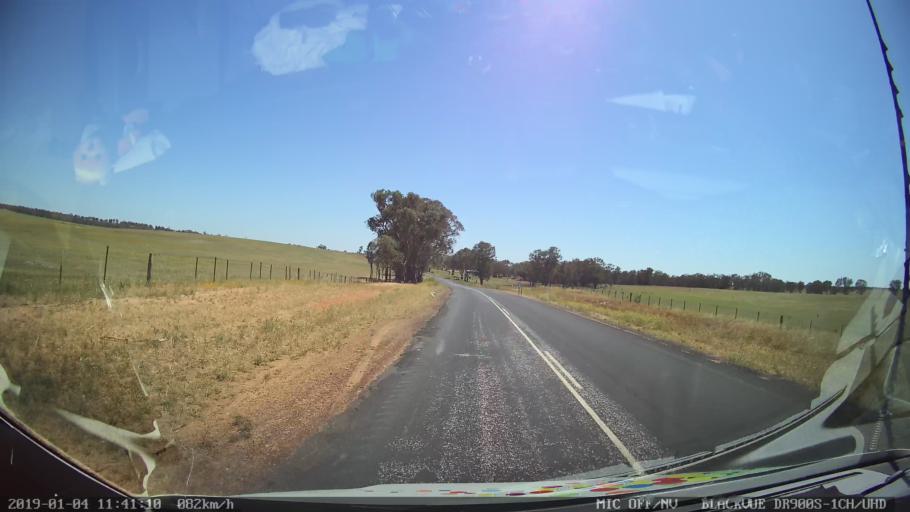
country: AU
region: New South Wales
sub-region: Cabonne
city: Molong
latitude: -32.9969
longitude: 148.7869
